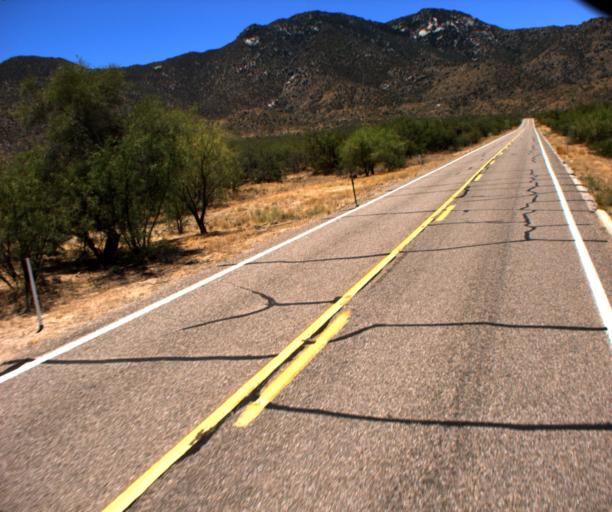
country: US
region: Arizona
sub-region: Pima County
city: Three Points
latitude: 31.9953
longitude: -111.5726
